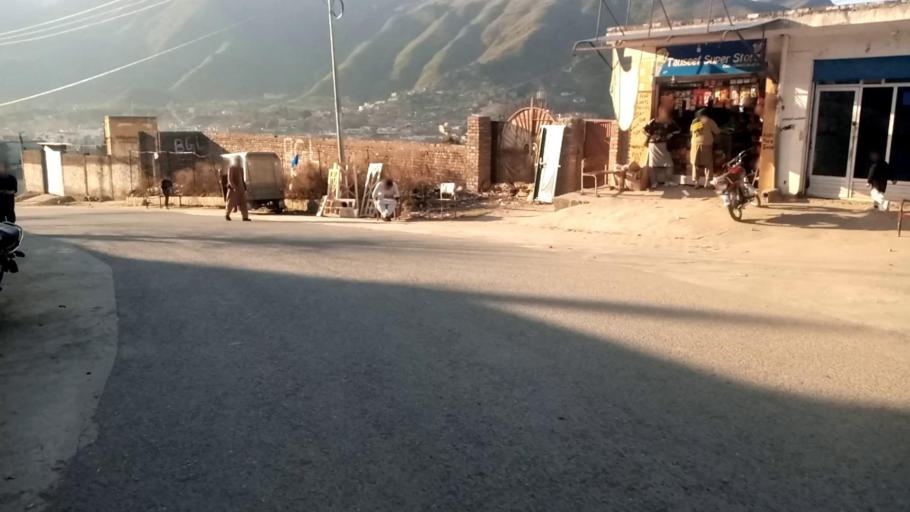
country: PK
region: Khyber Pakhtunkhwa
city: Saidu Sharif
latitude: 34.7437
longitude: 72.3529
